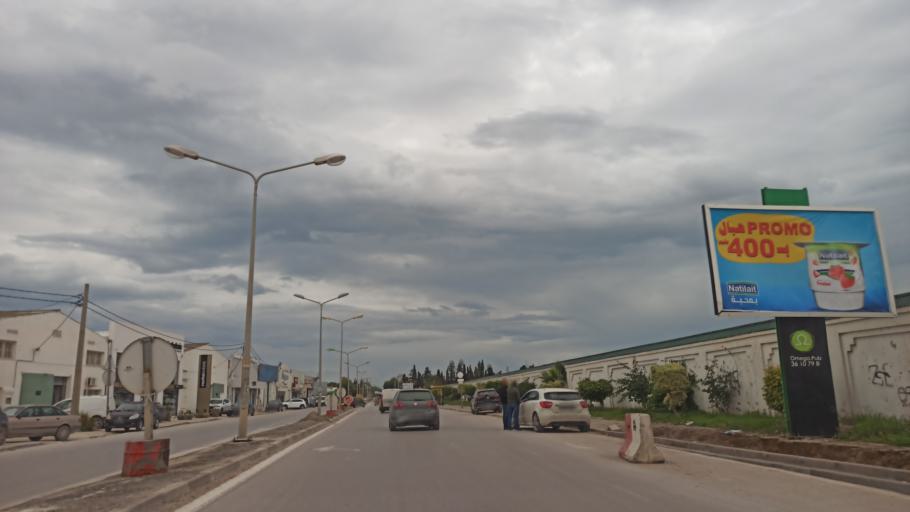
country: TN
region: Ariana
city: Ariana
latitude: 36.8703
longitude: 10.2311
